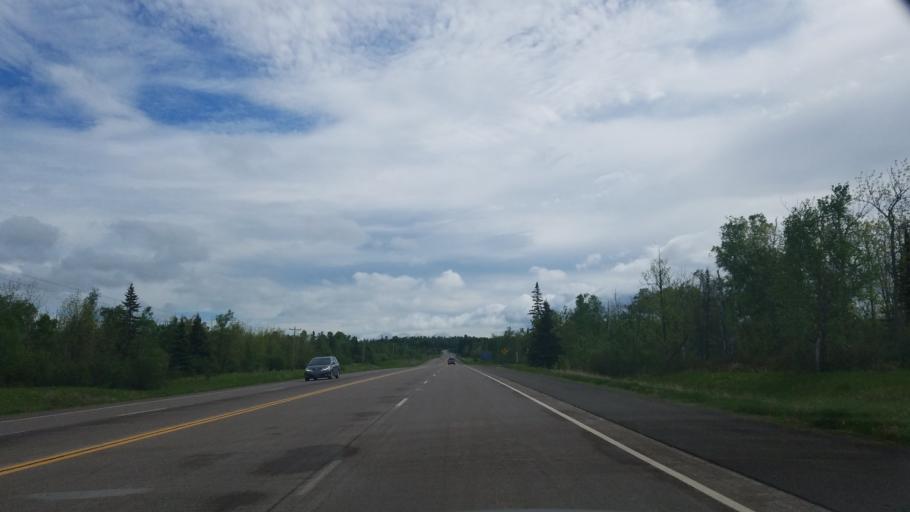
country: US
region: Minnesota
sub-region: Lake County
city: Two Harbors
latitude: 47.1327
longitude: -91.4831
